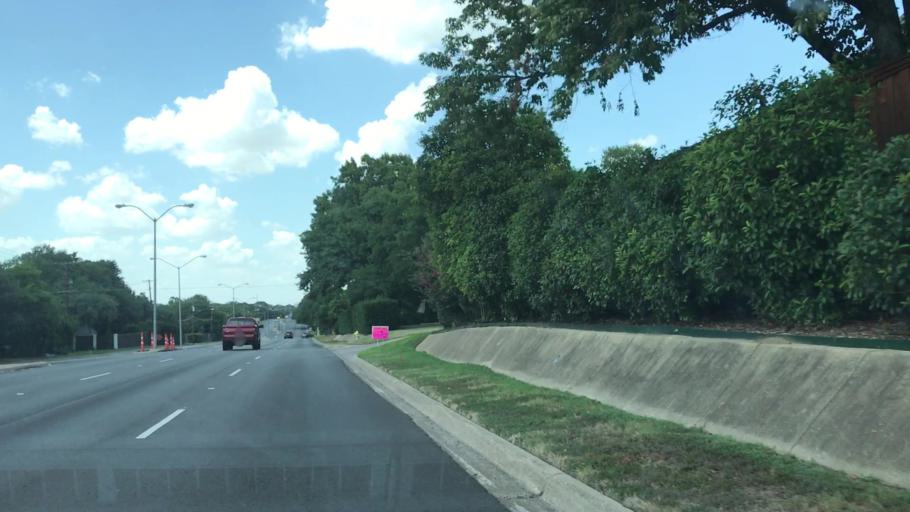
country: US
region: Texas
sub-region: Dallas County
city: Addison
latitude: 32.9040
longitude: -96.8382
